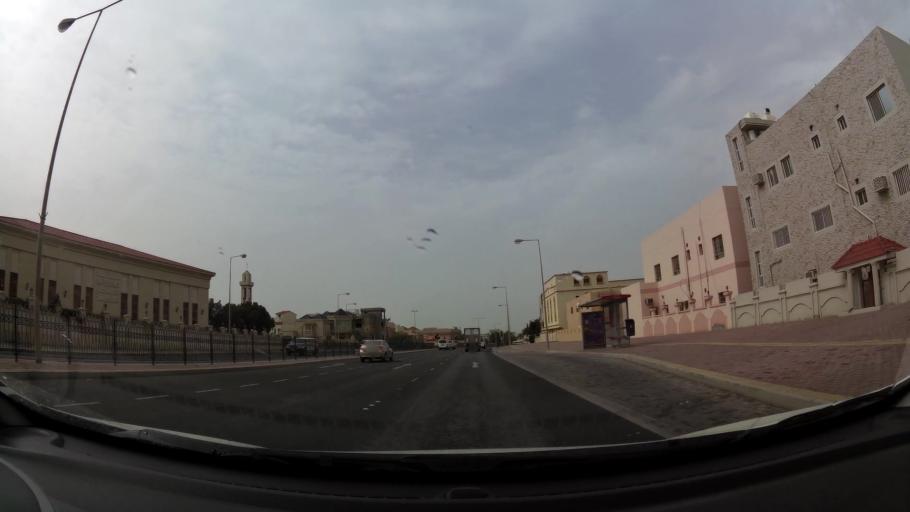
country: BH
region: Northern
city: Ar Rifa'
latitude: 26.1383
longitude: 50.5591
